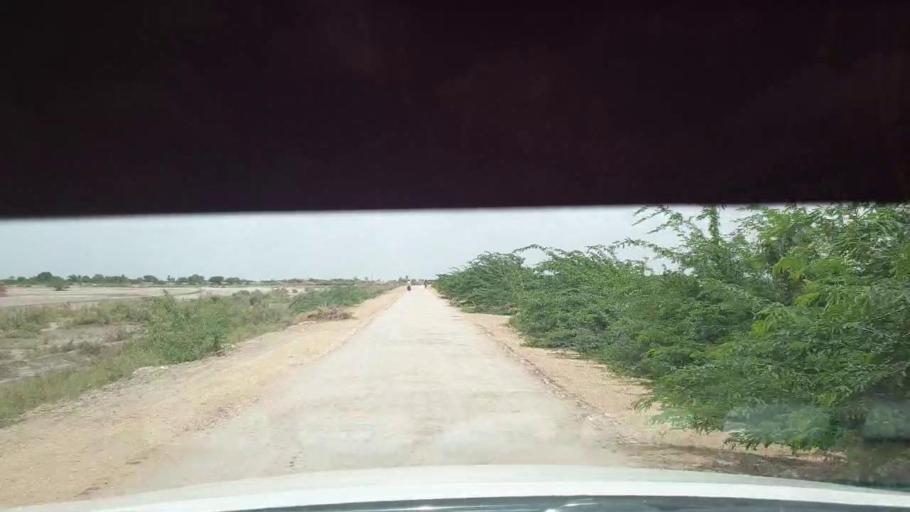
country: PK
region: Sindh
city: Kadhan
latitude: 24.4650
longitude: 69.0220
